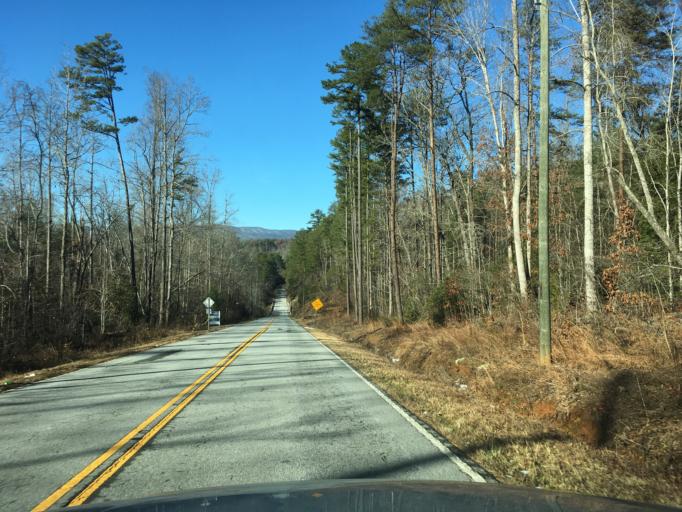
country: US
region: South Carolina
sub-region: Oconee County
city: Walhalla
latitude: 34.9265
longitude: -82.9863
